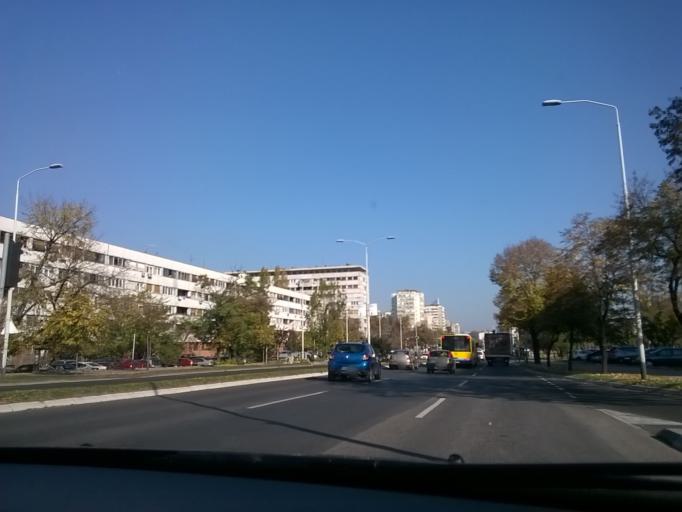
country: RS
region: Central Serbia
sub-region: Belgrade
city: Novi Beograd
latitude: 44.8191
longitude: 20.4088
